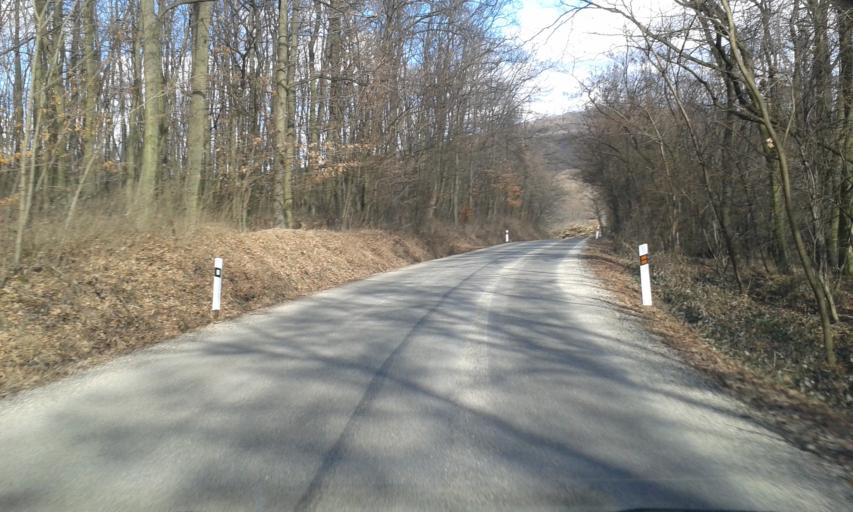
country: SK
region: Nitriansky
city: Zlate Moravce
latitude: 48.4455
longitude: 18.3258
